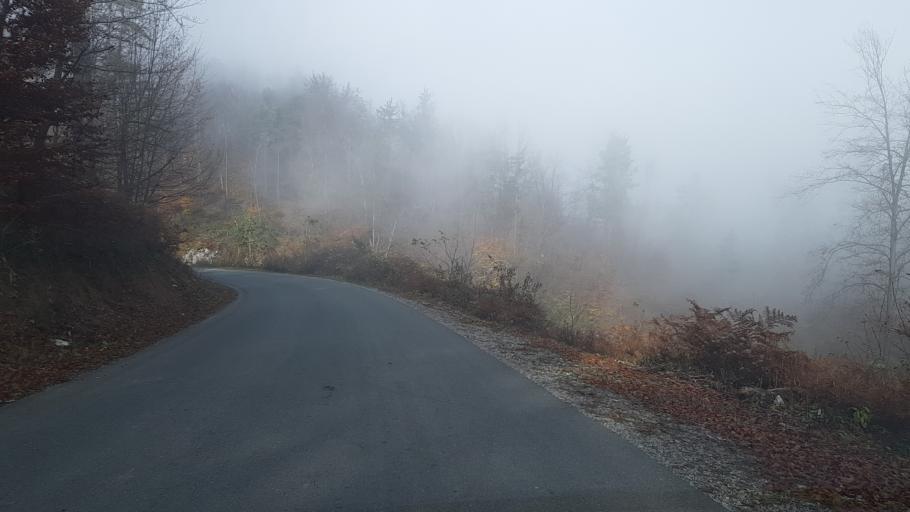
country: SI
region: Borovnica
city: Borovnica
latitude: 45.9084
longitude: 14.3646
